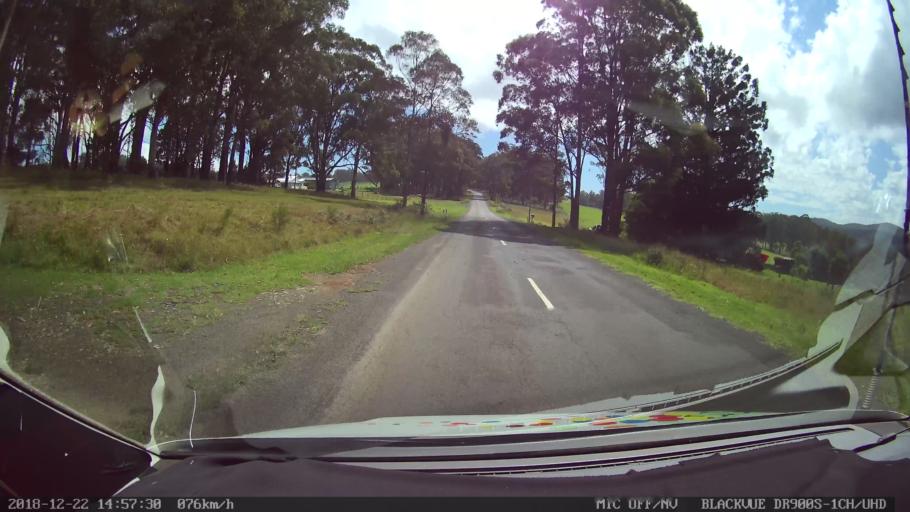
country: AU
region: New South Wales
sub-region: Bellingen
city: Dorrigo
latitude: -30.2347
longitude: 152.5005
